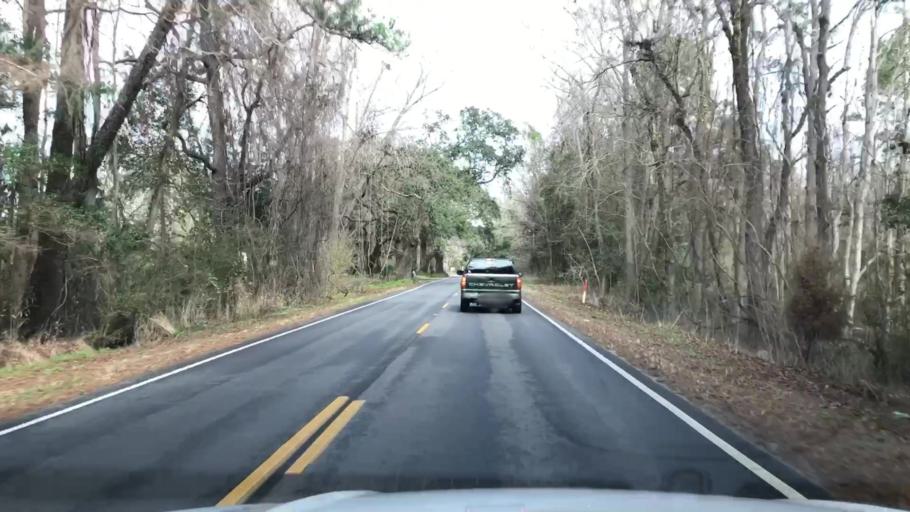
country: US
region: South Carolina
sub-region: Charleston County
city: Folly Beach
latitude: 32.6935
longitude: -80.0160
